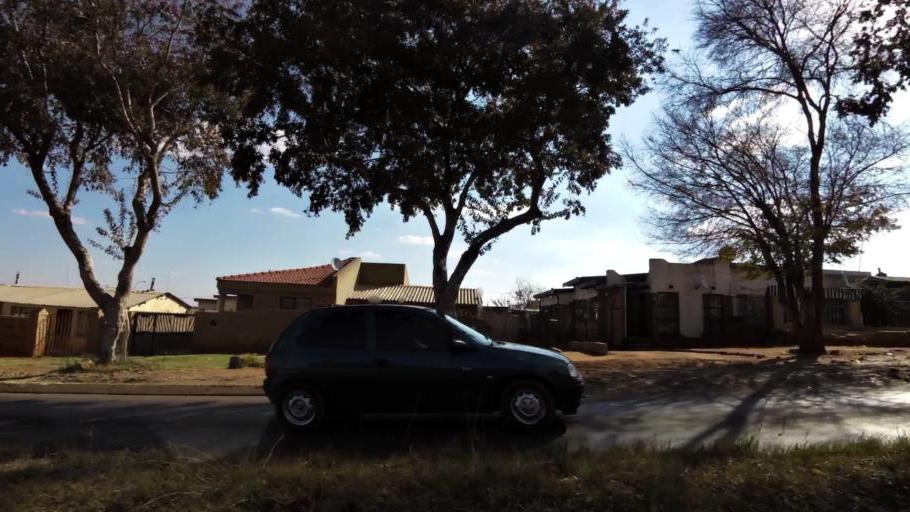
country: ZA
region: Gauteng
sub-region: City of Johannesburg Metropolitan Municipality
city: Soweto
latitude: -26.2203
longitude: 27.8892
